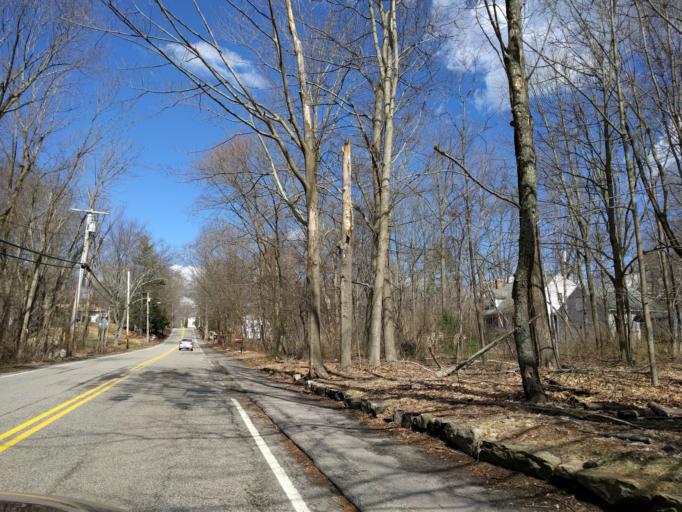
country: US
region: Massachusetts
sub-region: Norfolk County
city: Medway
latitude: 42.1404
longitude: -71.4316
